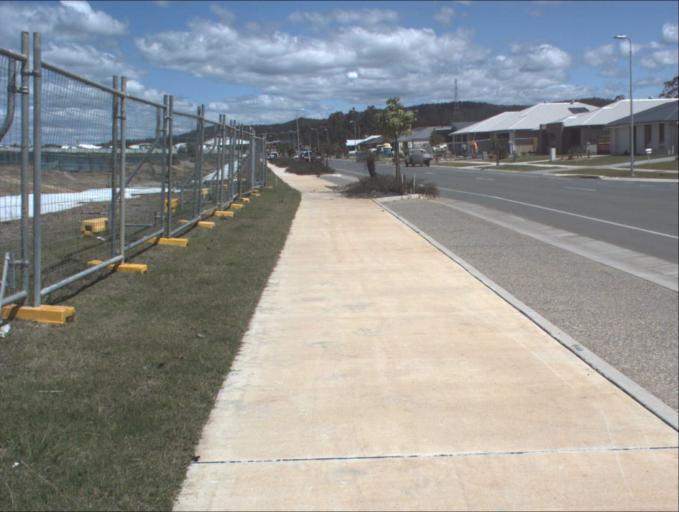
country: AU
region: Queensland
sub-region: Logan
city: Chambers Flat
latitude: -27.8025
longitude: 153.1132
